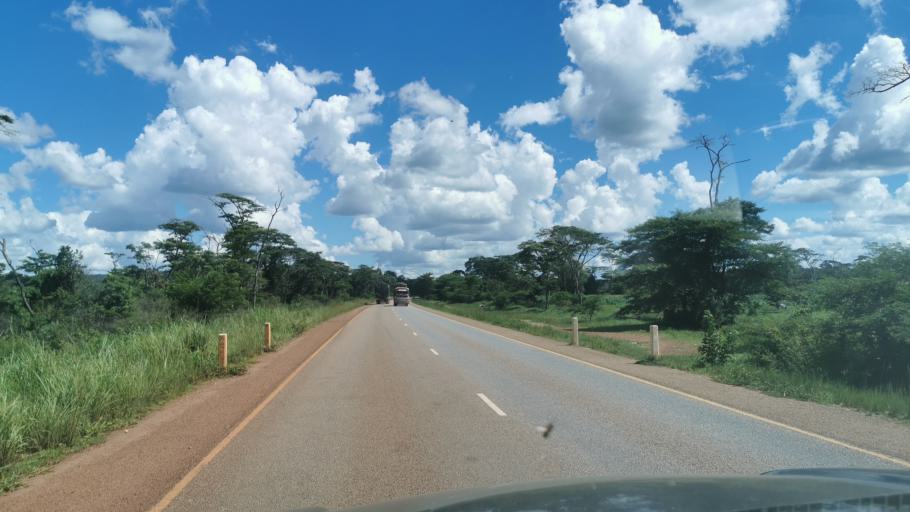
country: TZ
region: Geita
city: Uyovu
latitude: -3.0487
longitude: 31.2522
